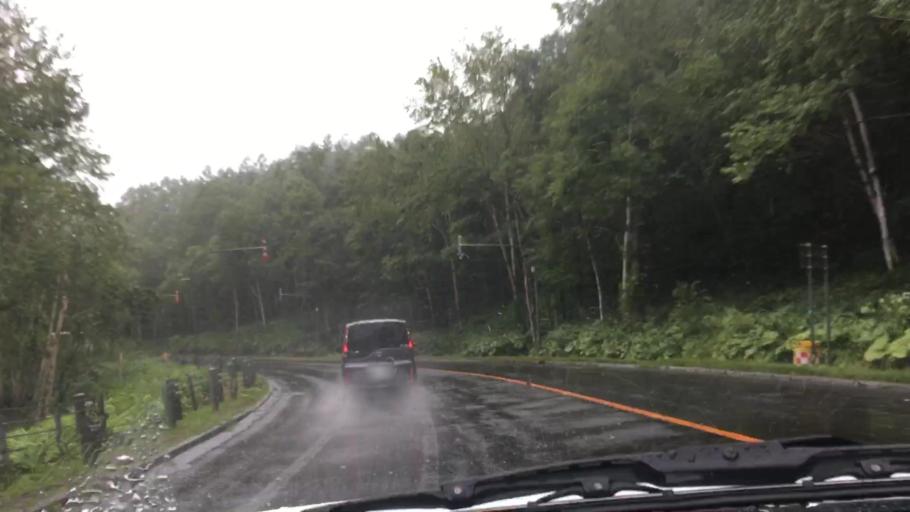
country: JP
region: Hokkaido
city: Sapporo
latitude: 42.8834
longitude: 141.1401
